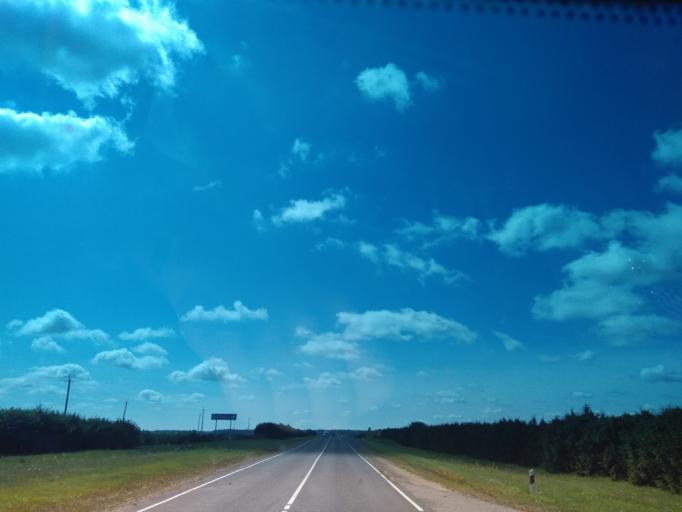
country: BY
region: Minsk
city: Uzda
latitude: 53.3758
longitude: 27.2364
